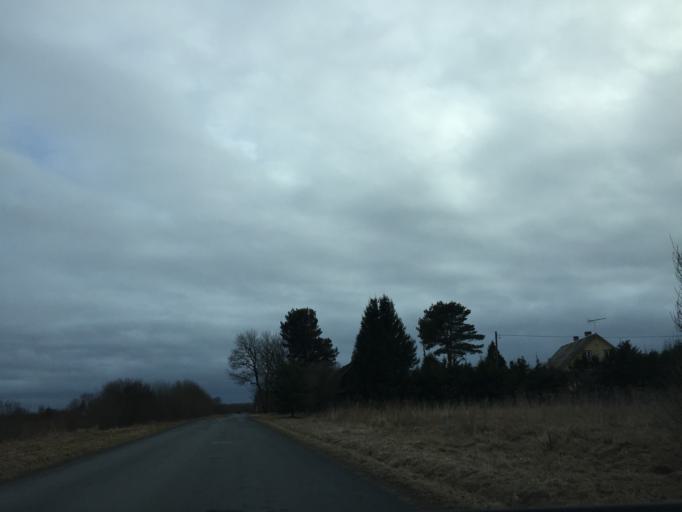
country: EE
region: Laeaene
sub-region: Haapsalu linn
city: Haapsalu
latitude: 58.8117
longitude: 23.5496
